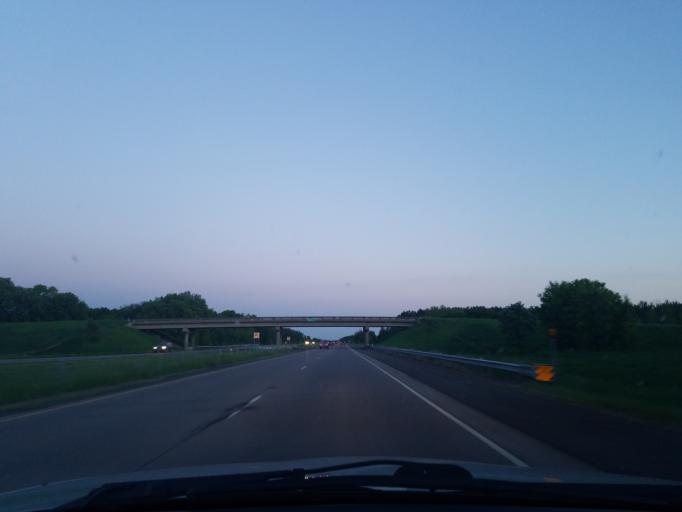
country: US
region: Minnesota
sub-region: Chisago County
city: Rush City
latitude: 45.7179
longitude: -92.9924
